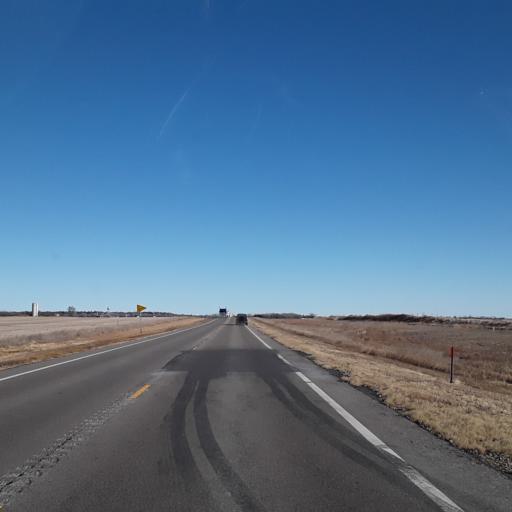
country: US
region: Kansas
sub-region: Pawnee County
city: Larned
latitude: 38.1477
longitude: -99.1393
